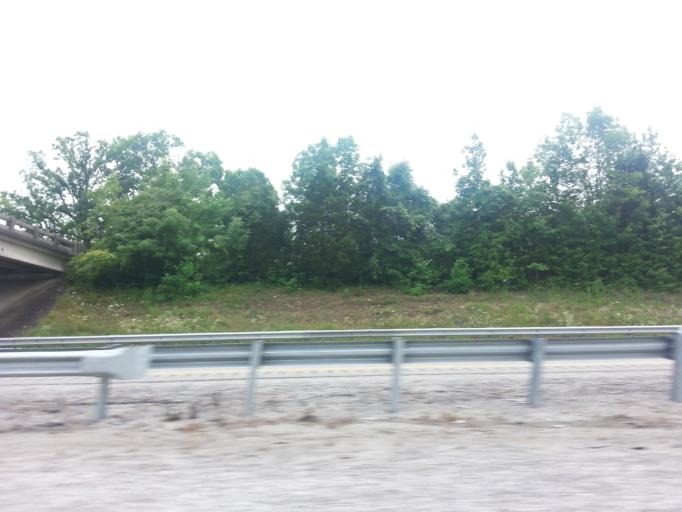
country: US
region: Tennessee
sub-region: Putnam County
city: Monterey
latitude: 36.1362
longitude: -85.3249
